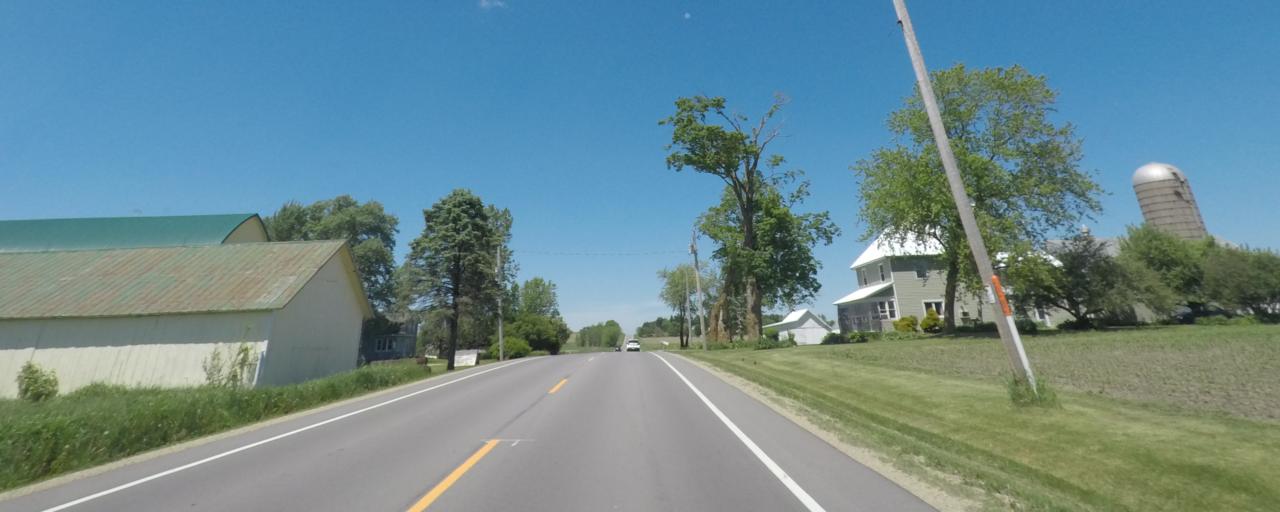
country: US
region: Wisconsin
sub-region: Green County
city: Brooklyn
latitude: 42.8156
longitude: -89.3692
